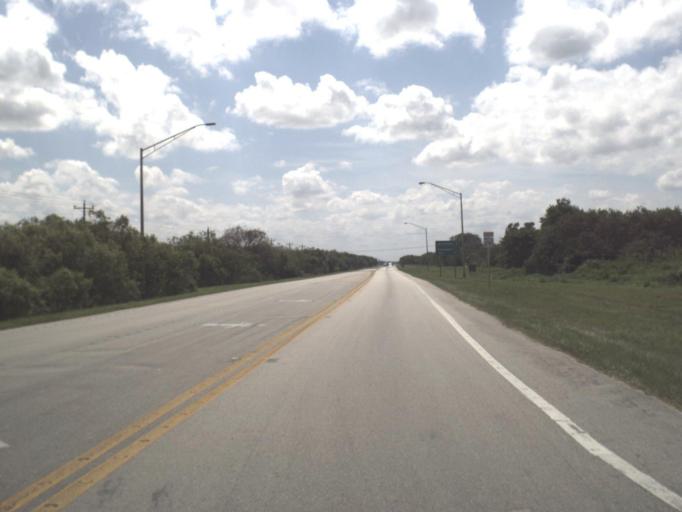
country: US
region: Florida
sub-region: Collier County
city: Immokalee
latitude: 26.4854
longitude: -81.4347
